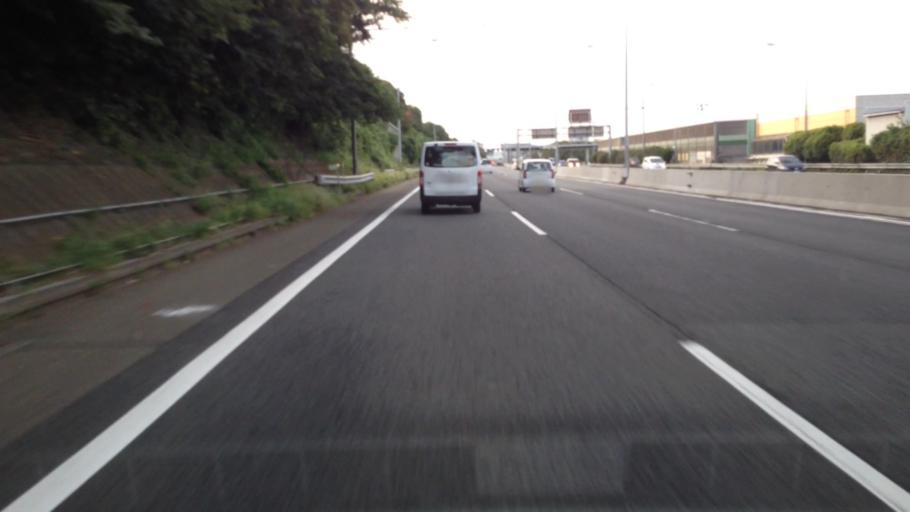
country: JP
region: Kanagawa
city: Yokohama
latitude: 35.4812
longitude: 139.5948
